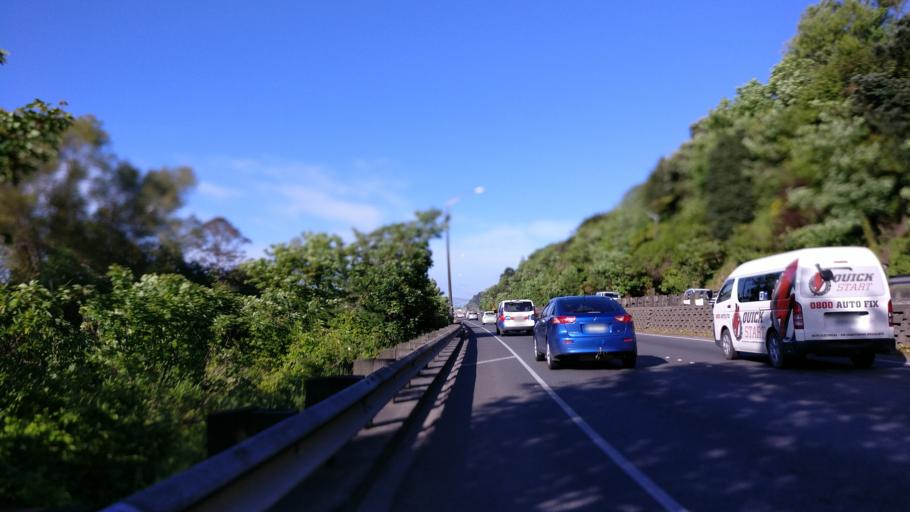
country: NZ
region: Wellington
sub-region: Lower Hutt City
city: Lower Hutt
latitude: -41.1994
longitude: 174.9130
